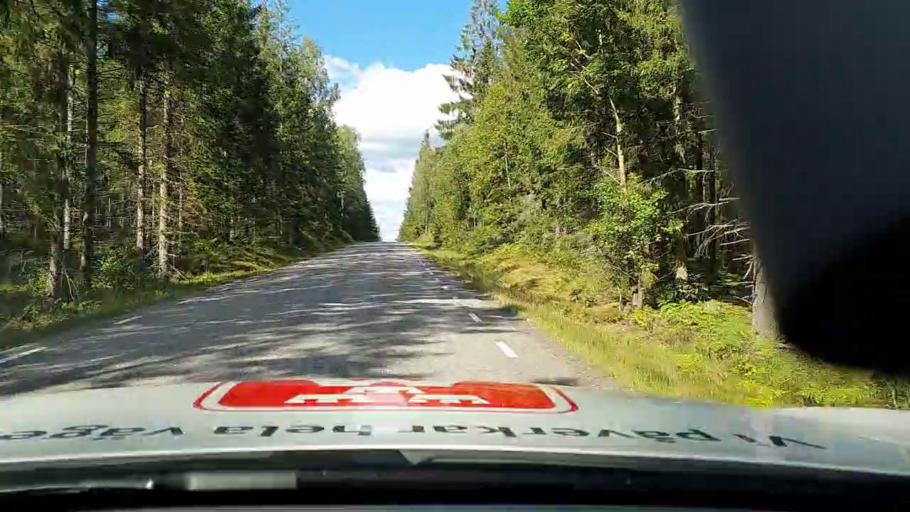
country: SE
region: Vaestra Goetaland
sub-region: Marks Kommun
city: Fritsla
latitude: 57.3843
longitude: 12.8570
